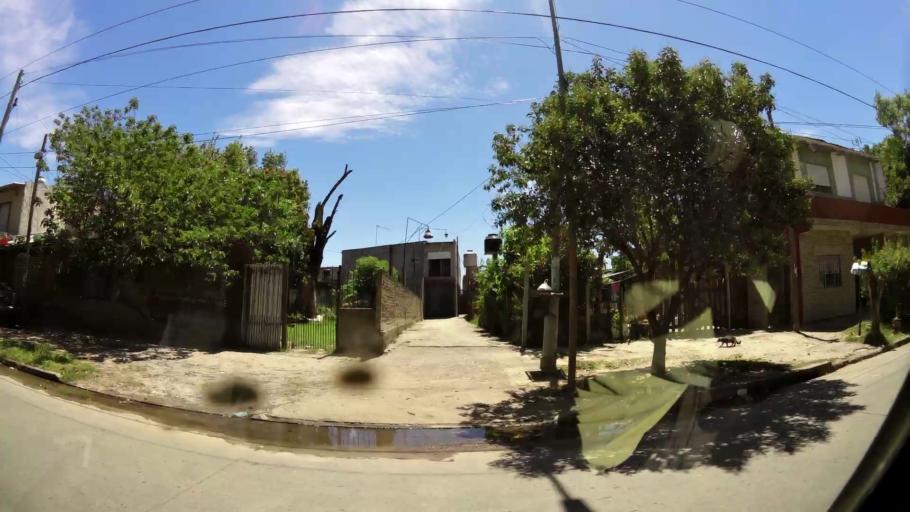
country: AR
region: Buenos Aires
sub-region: Partido de Quilmes
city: Quilmes
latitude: -34.7323
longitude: -58.3238
